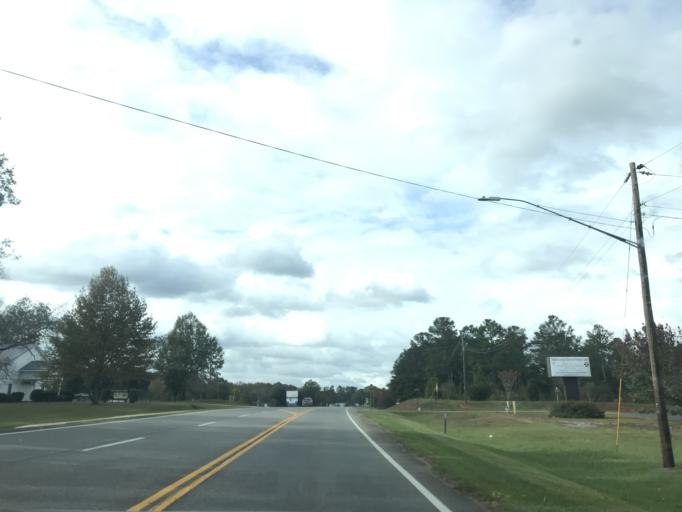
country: US
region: Georgia
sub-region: Jones County
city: Gray
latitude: 32.9987
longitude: -83.5288
